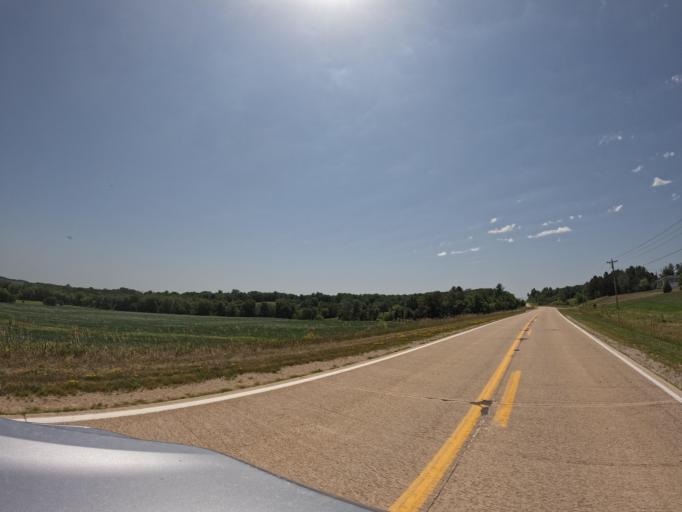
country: US
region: Iowa
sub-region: Henry County
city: Mount Pleasant
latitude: 40.9200
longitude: -91.5539
